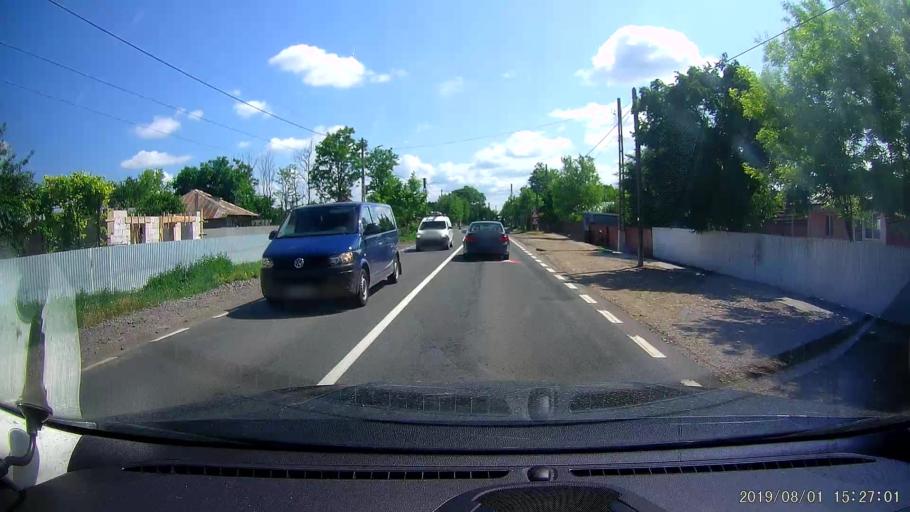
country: RO
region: Braila
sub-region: Comuna Viziru
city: Viziru
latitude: 45.0047
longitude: 27.7173
